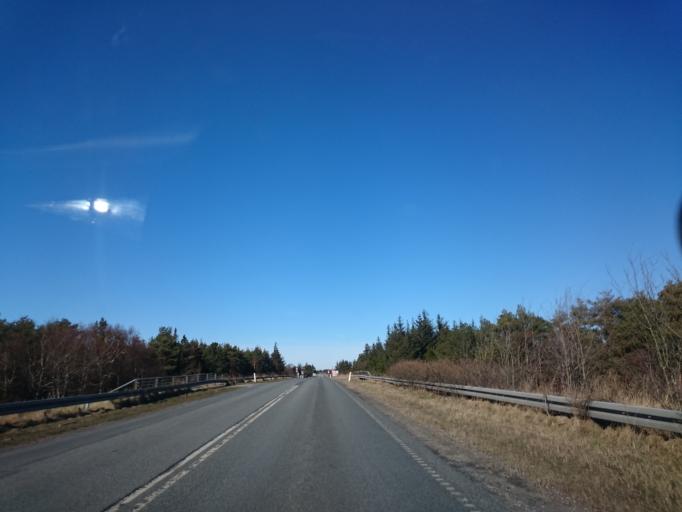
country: DK
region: North Denmark
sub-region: Frederikshavn Kommune
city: Skagen
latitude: 57.6537
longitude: 10.4591
